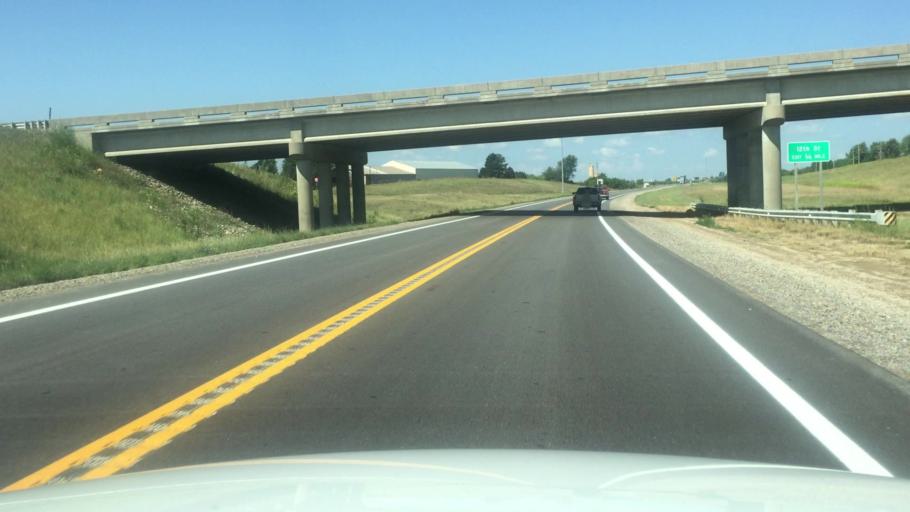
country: US
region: Kansas
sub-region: Brown County
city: Hiawatha
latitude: 39.8409
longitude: -95.5265
